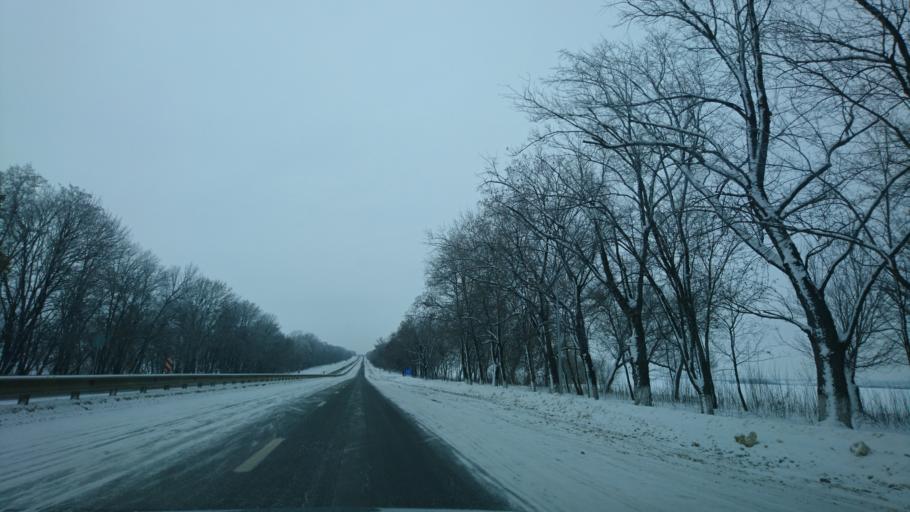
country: RU
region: Belgorod
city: Mayskiy
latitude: 50.4333
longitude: 36.3878
